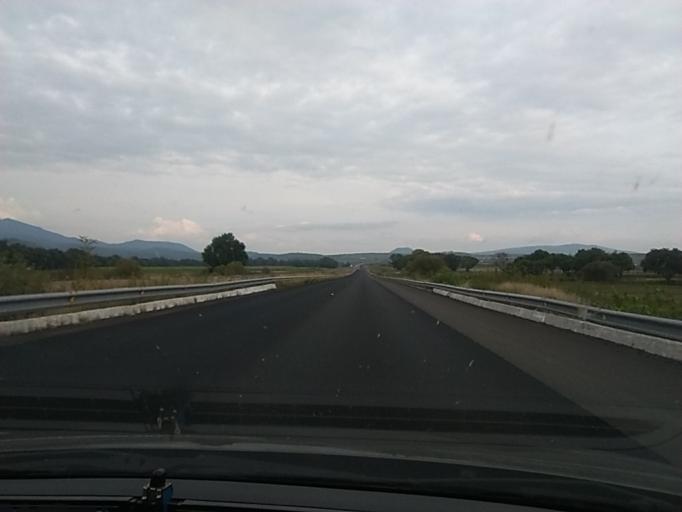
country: MX
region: Mexico
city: Huaniqueo de Morales
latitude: 19.8928
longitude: -101.5387
